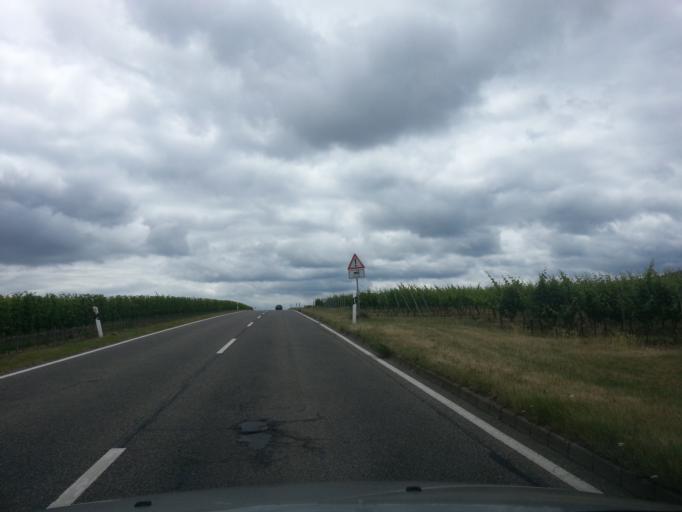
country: DE
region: Rheinland-Pfalz
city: Weisenheim am Berg
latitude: 49.5060
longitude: 8.1584
